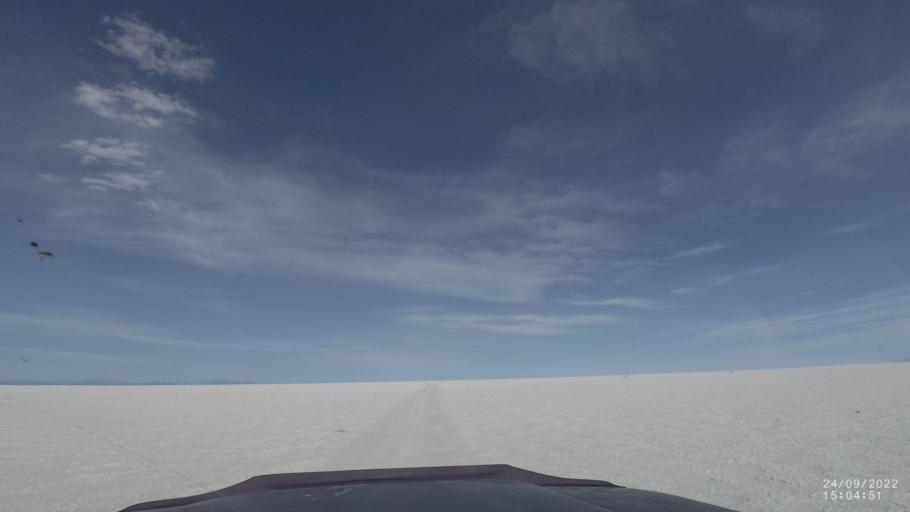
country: BO
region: Potosi
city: Colchani
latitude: -19.9020
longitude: -67.5218
